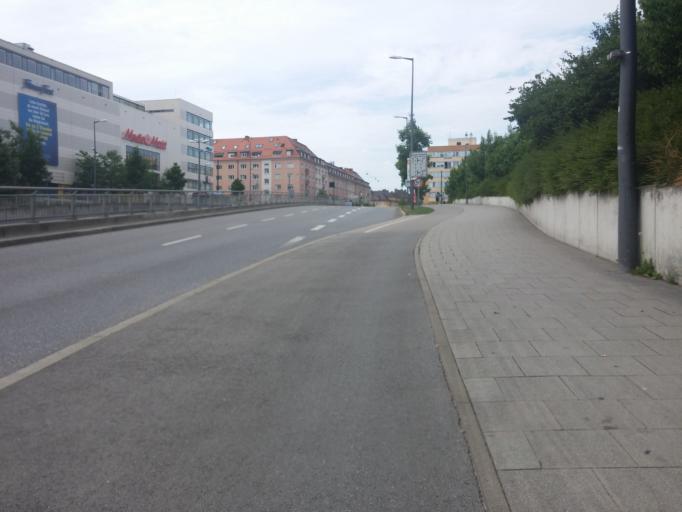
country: DE
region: Bavaria
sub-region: Upper Bavaria
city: Bogenhausen
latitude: 48.1356
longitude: 11.6156
